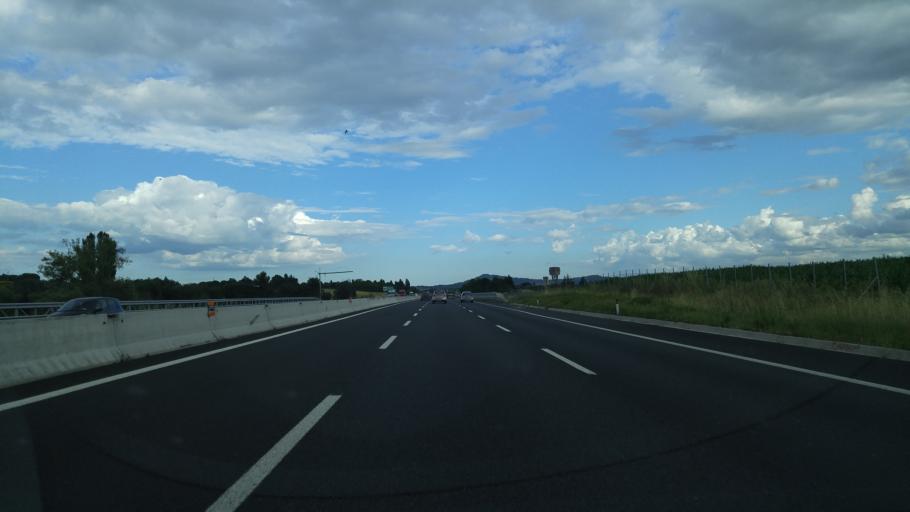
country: IT
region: Emilia-Romagna
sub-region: Provincia di Rimini
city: Santa Monica-Cella
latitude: 43.9617
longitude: 12.6957
